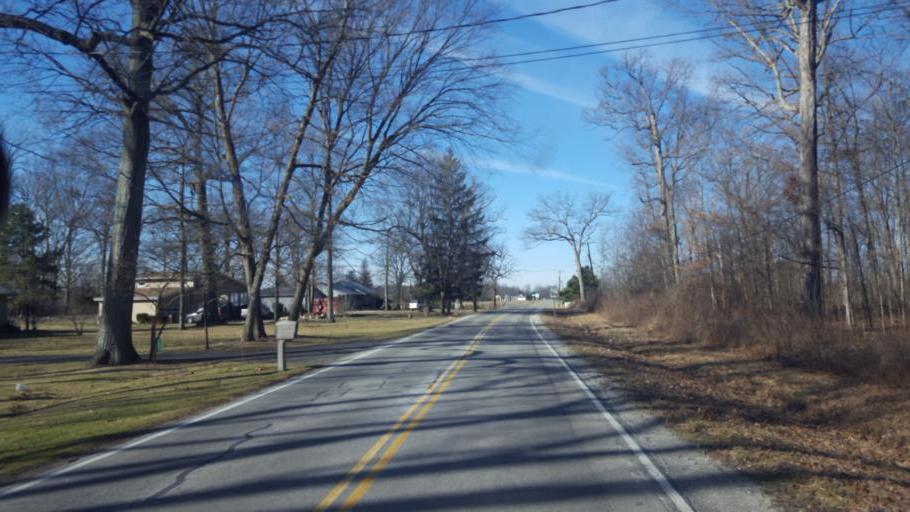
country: US
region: Ohio
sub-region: Marion County
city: Marion
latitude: 40.5351
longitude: -83.0771
